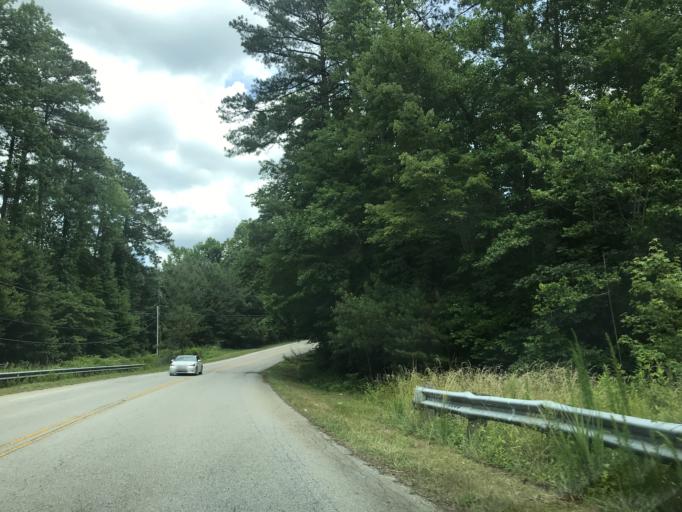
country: US
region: North Carolina
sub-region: Wake County
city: West Raleigh
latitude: 35.9134
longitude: -78.6788
